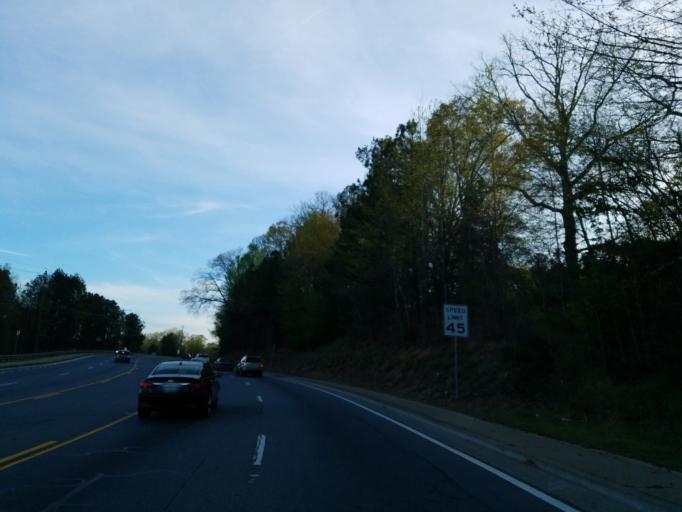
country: US
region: Georgia
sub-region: Cherokee County
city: Canton
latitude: 34.2416
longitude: -84.4980
